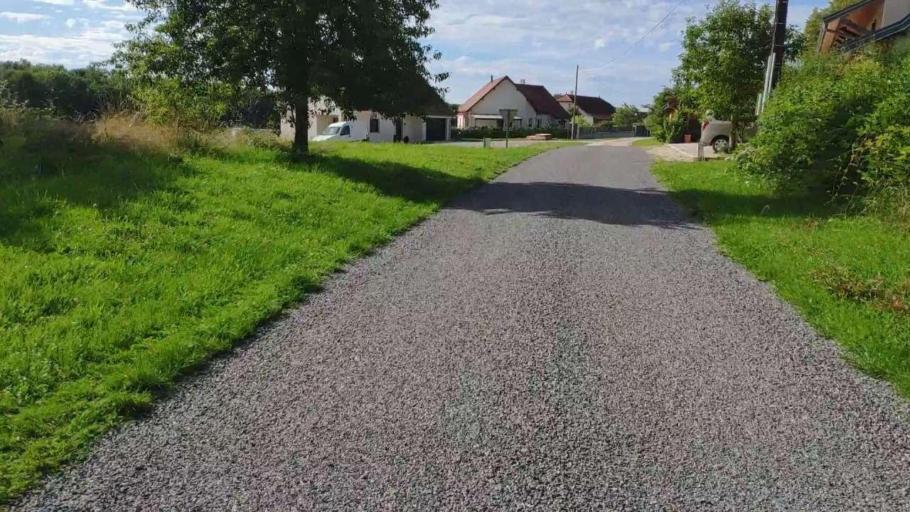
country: FR
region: Franche-Comte
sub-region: Departement du Jura
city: Bletterans
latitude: 46.8262
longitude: 5.5286
